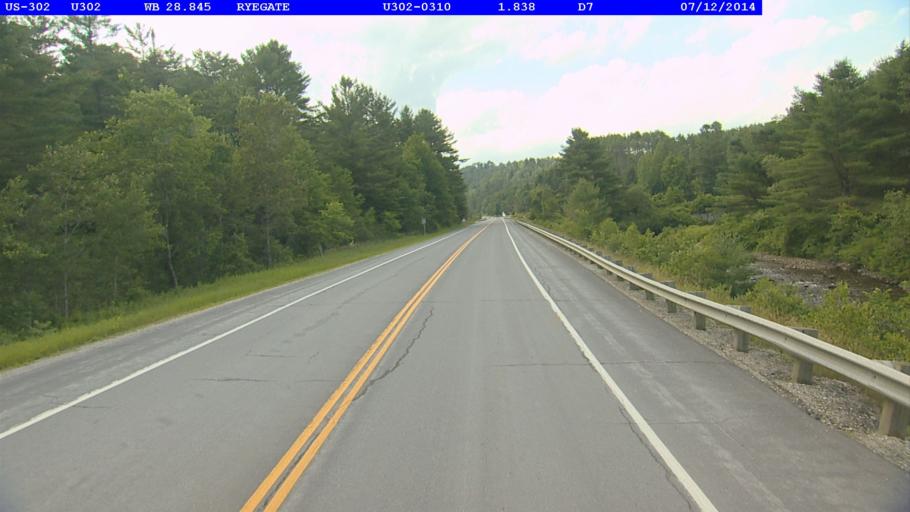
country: US
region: New Hampshire
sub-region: Grafton County
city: Woodsville
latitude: 44.1886
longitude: -72.1449
